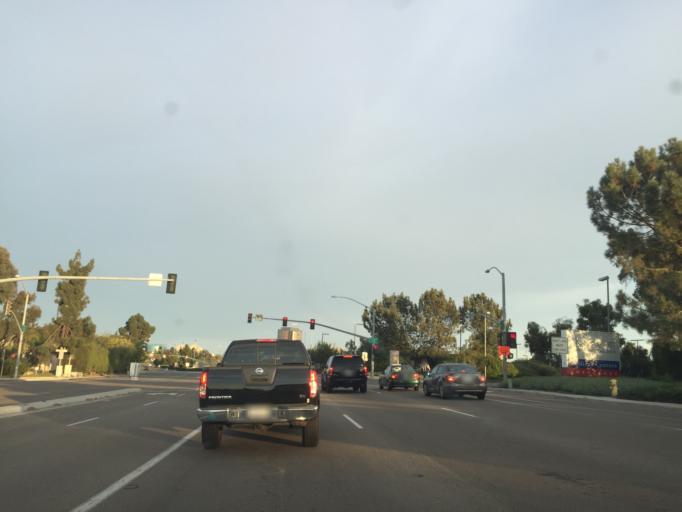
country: US
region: California
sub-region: San Diego County
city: La Jolla
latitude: 32.8824
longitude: -117.2208
